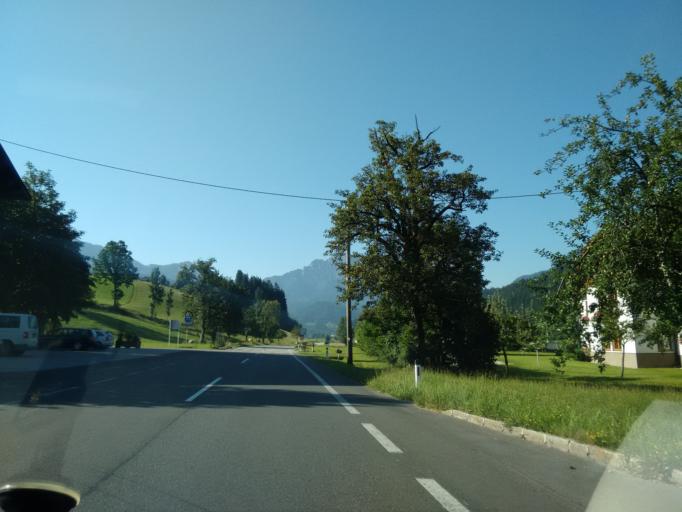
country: AT
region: Upper Austria
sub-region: Politischer Bezirk Kirchdorf an der Krems
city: Rossleithen
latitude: 47.6951
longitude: 14.3470
